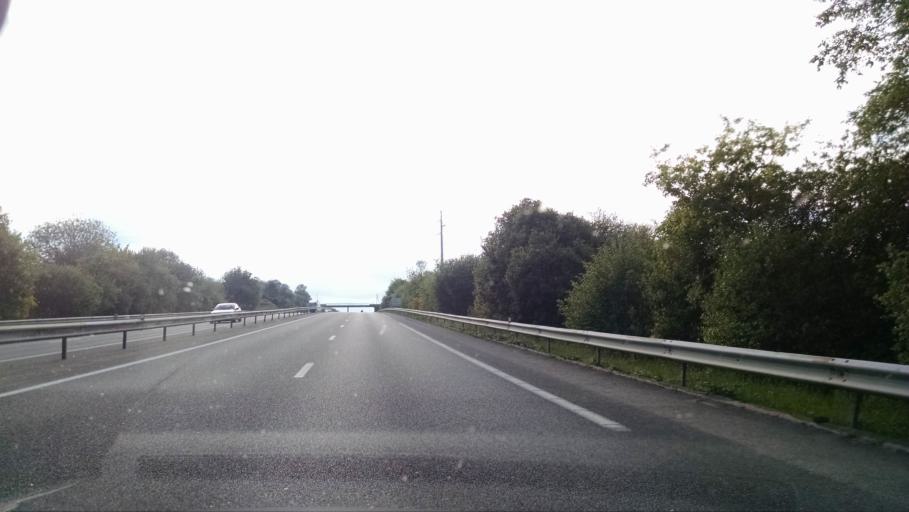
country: FR
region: Brittany
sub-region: Departement du Finistere
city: Guerlesquin
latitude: 48.5676
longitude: -3.5830
